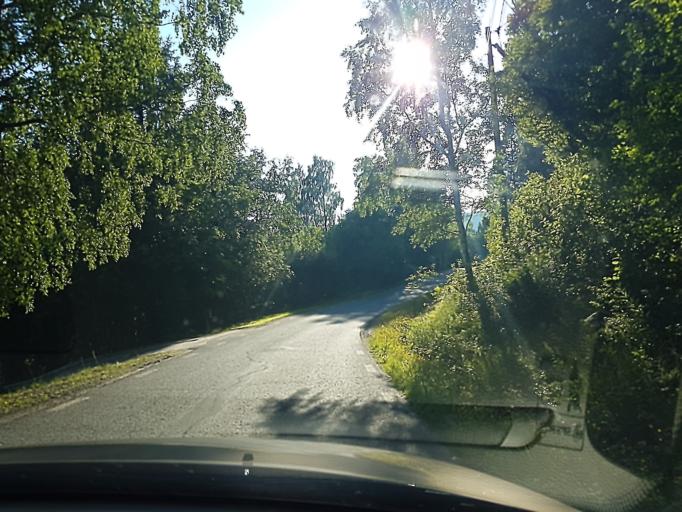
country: SE
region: Vaesternorrland
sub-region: Kramfors Kommun
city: Nordingra
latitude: 63.0607
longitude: 18.3981
